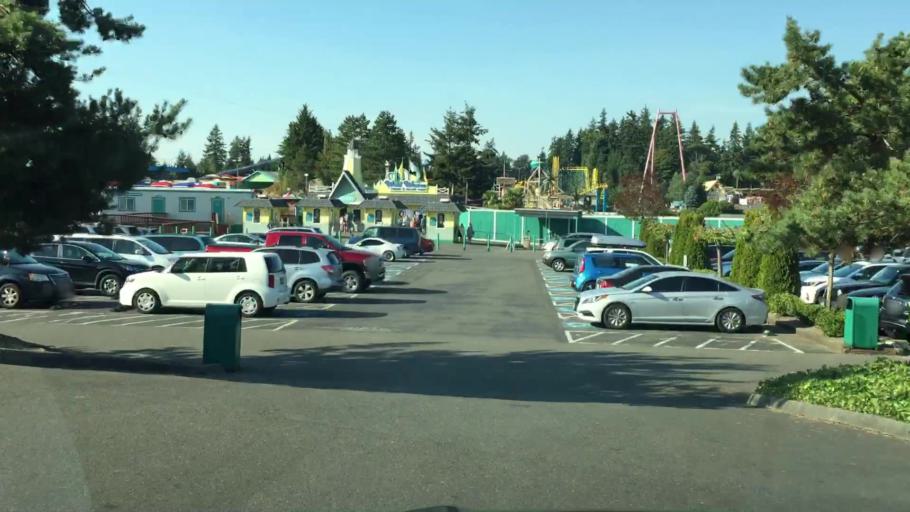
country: US
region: Washington
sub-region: Pierce County
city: Milton
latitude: 47.2716
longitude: -122.3116
